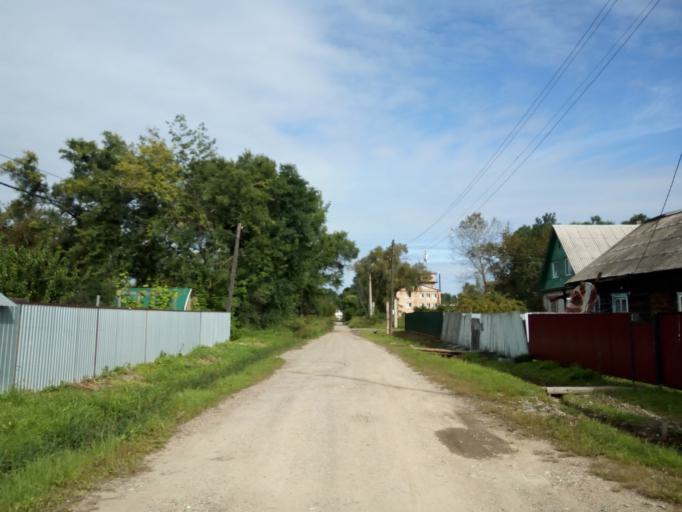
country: RU
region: Primorskiy
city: Dal'nerechensk
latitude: 45.9342
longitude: 133.7470
